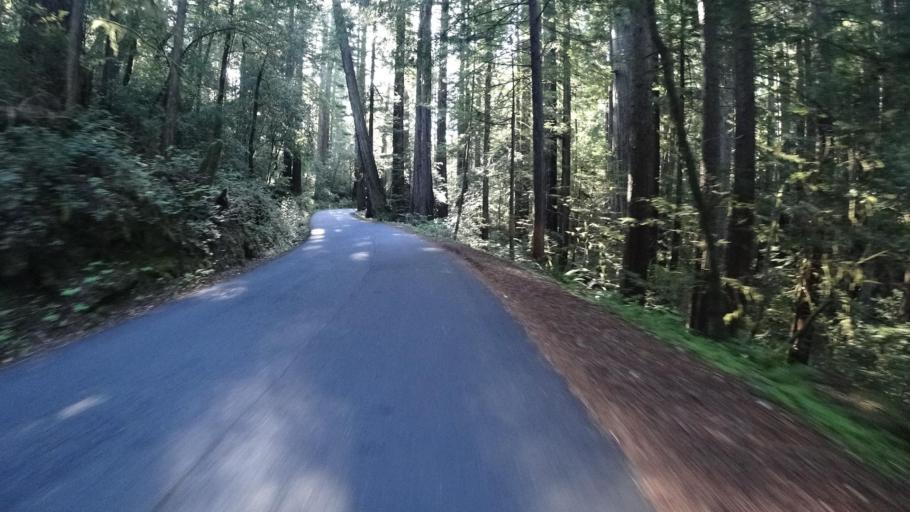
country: US
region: California
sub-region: Humboldt County
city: Rio Dell
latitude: 40.3433
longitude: -123.9511
